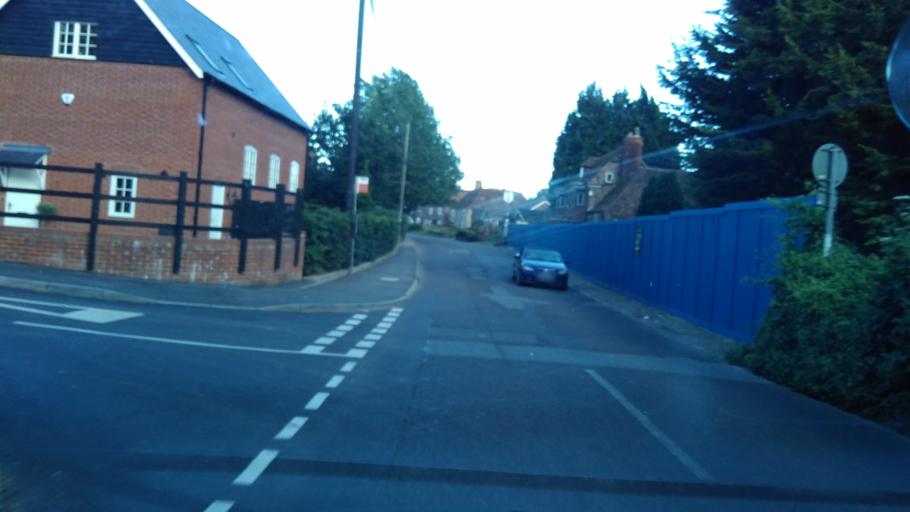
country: GB
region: England
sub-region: Kent
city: Chartham
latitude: 51.2546
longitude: 0.9956
